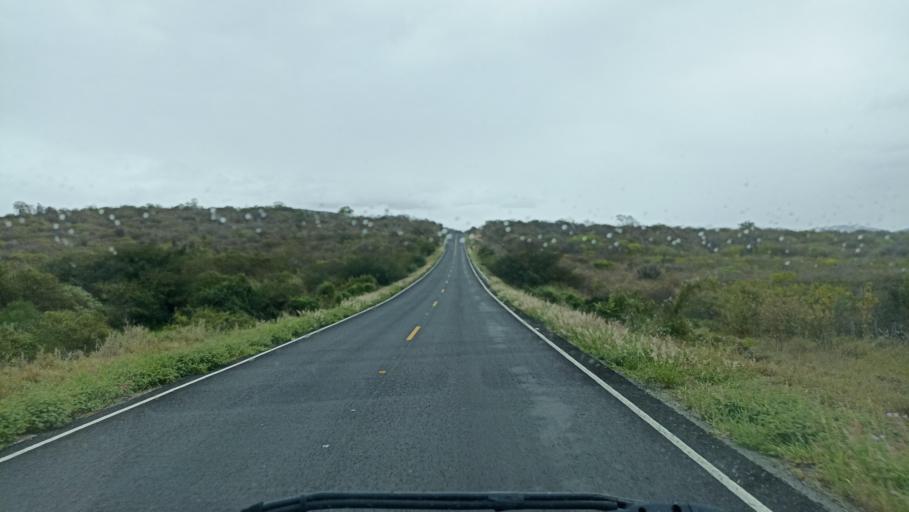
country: BR
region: Bahia
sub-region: Andarai
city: Vera Cruz
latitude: -13.0471
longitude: -40.7641
